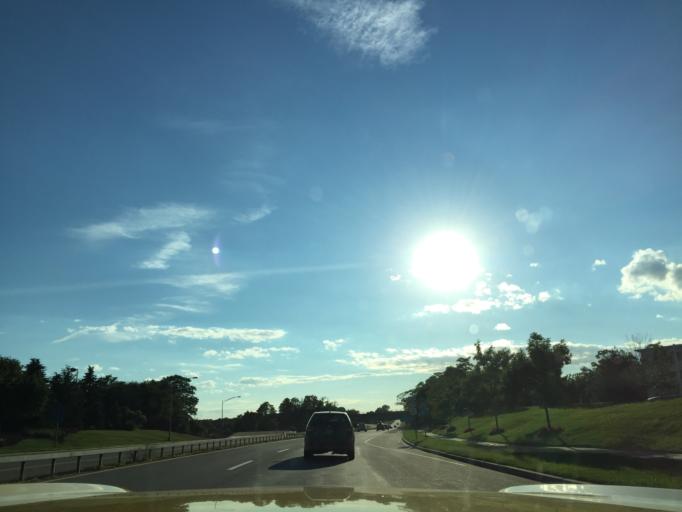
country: US
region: New York
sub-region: Suffolk County
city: Calverton
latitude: 40.9225
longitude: -72.7157
